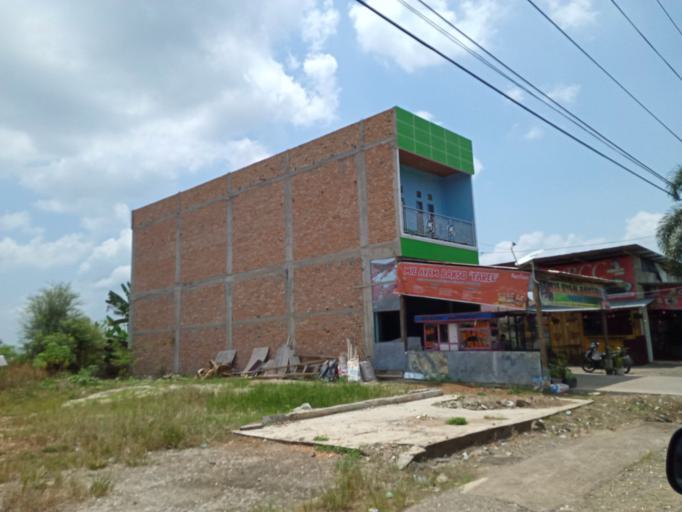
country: ID
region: Jambi
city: Bangko
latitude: -2.0857
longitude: 102.2591
